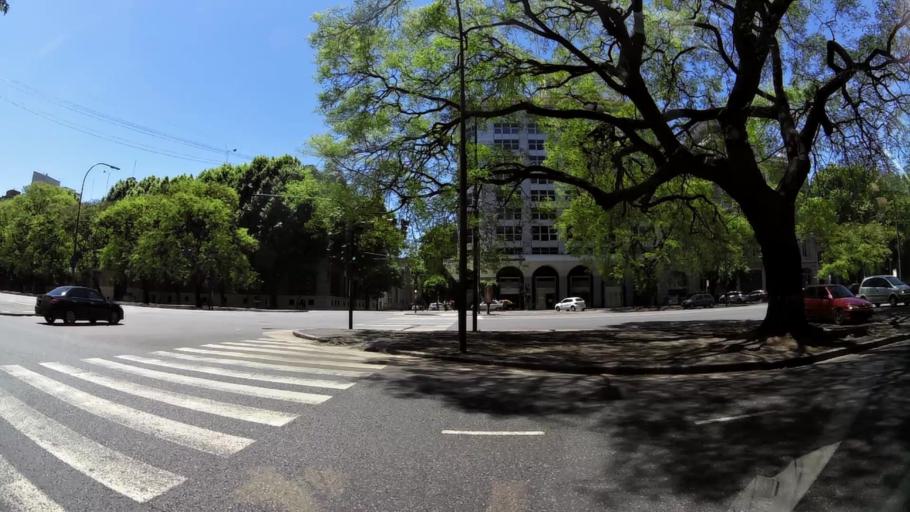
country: AR
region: Buenos Aires F.D.
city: Buenos Aires
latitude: -34.6159
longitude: -58.3695
